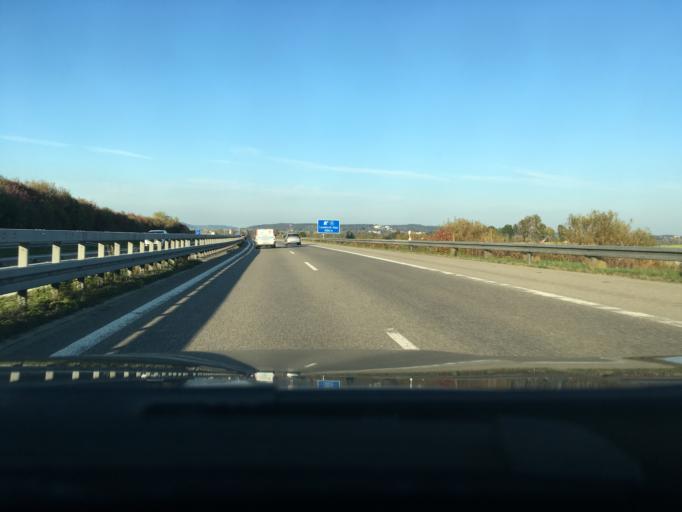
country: DE
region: Baden-Wuerttemberg
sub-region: Tuebingen Region
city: Leutkirch im Allgau
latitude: 47.8037
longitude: 9.9861
